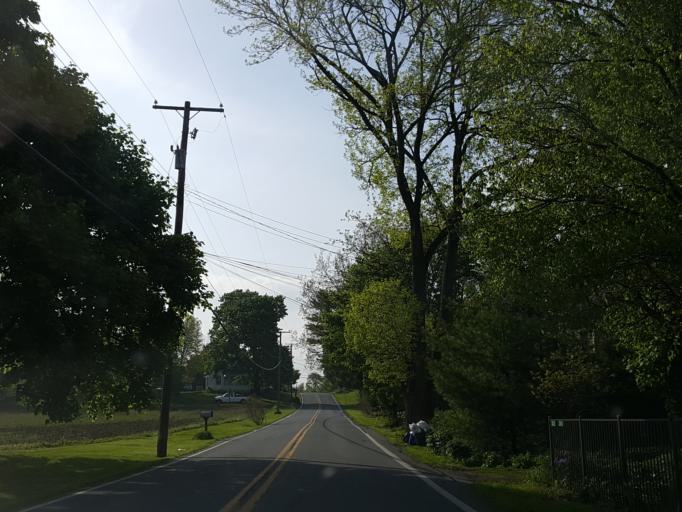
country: US
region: Pennsylvania
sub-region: Lebanon County
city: Campbelltown
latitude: 40.2411
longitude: -76.5922
